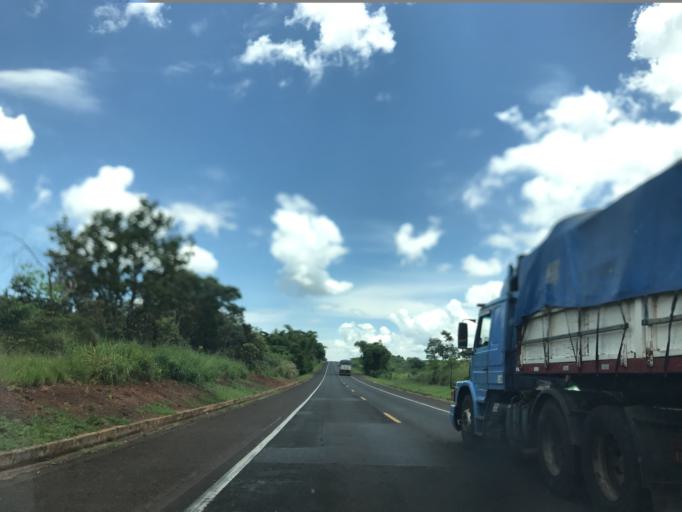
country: BR
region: Minas Gerais
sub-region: Prata
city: Prata
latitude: -19.5059
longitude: -48.8472
